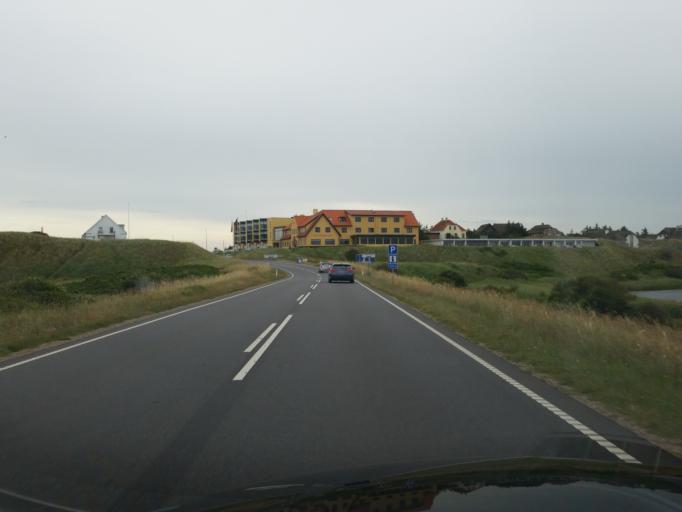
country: DK
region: Central Jutland
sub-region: Ringkobing-Skjern Kommune
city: Hvide Sande
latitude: 55.8174
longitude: 8.1886
